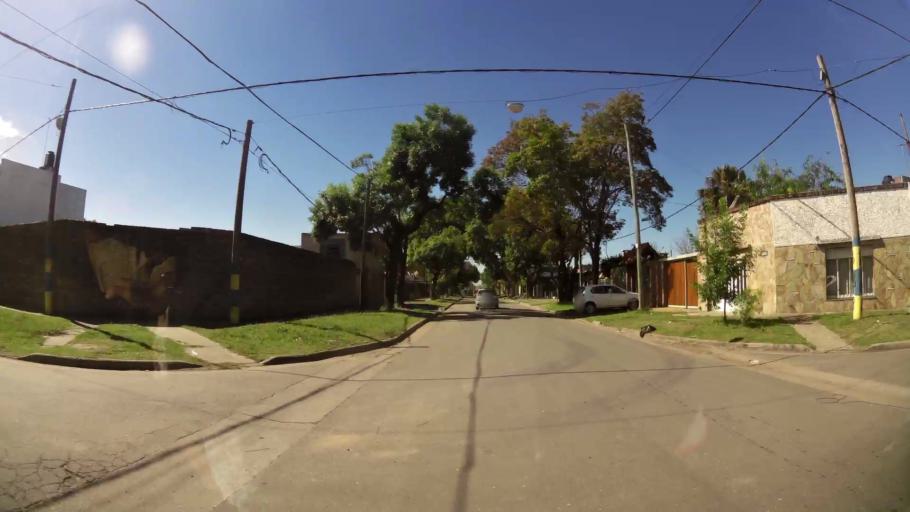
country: AR
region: Santa Fe
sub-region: Departamento de Rosario
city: Rosario
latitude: -32.9356
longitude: -60.7083
